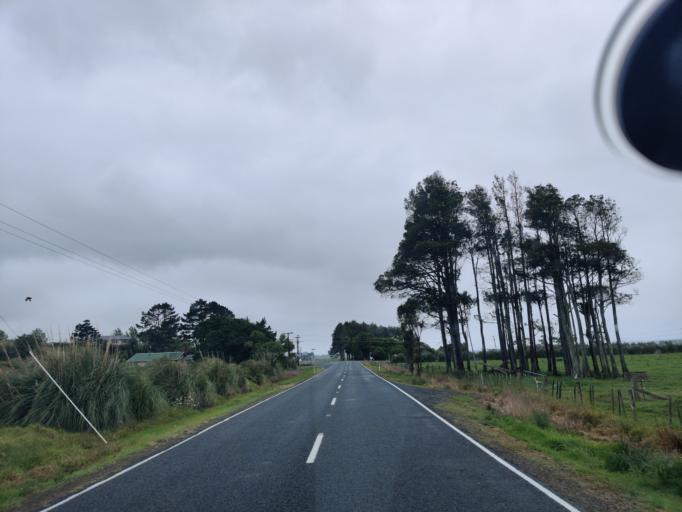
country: NZ
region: Northland
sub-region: Kaipara District
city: Dargaville
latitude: -36.0132
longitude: 173.9319
